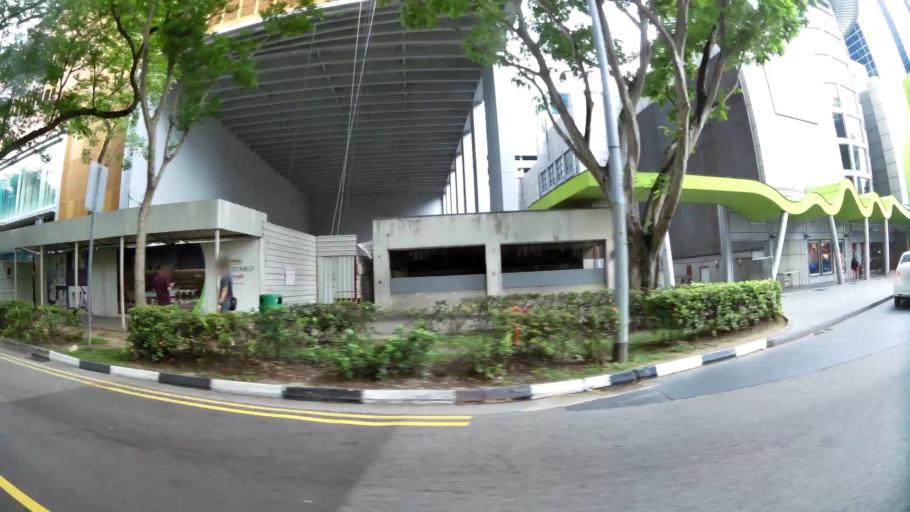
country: SG
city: Singapore
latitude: 1.3201
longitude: 103.8431
